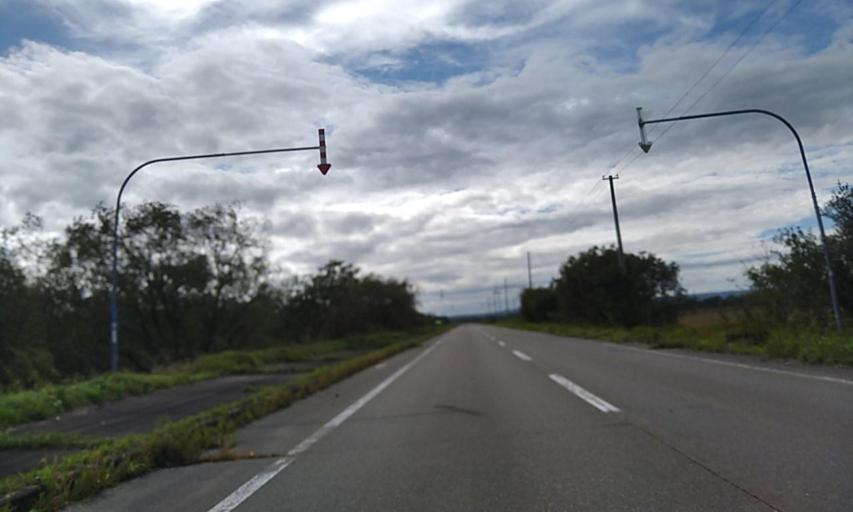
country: JP
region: Hokkaido
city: Obihiro
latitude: 42.7240
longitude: 143.6656
